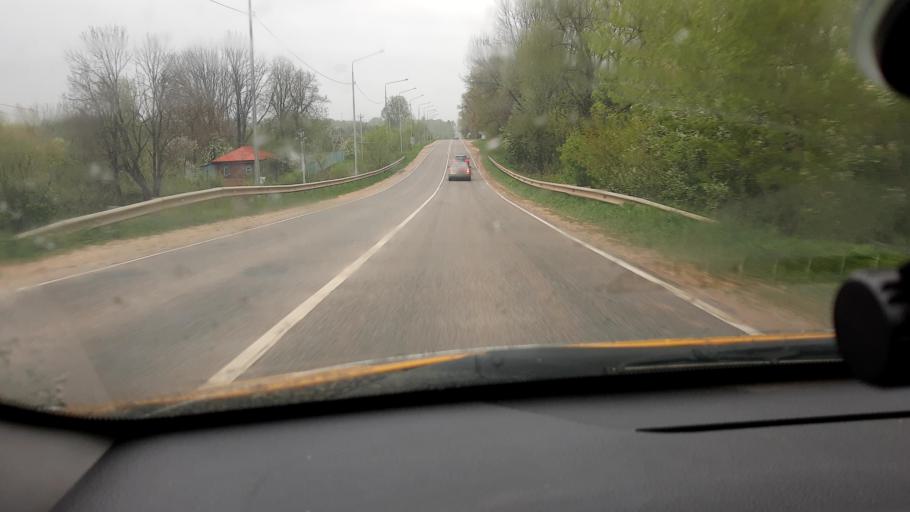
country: RU
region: Tula
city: Zaokskiy
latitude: 54.7633
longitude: 37.4369
